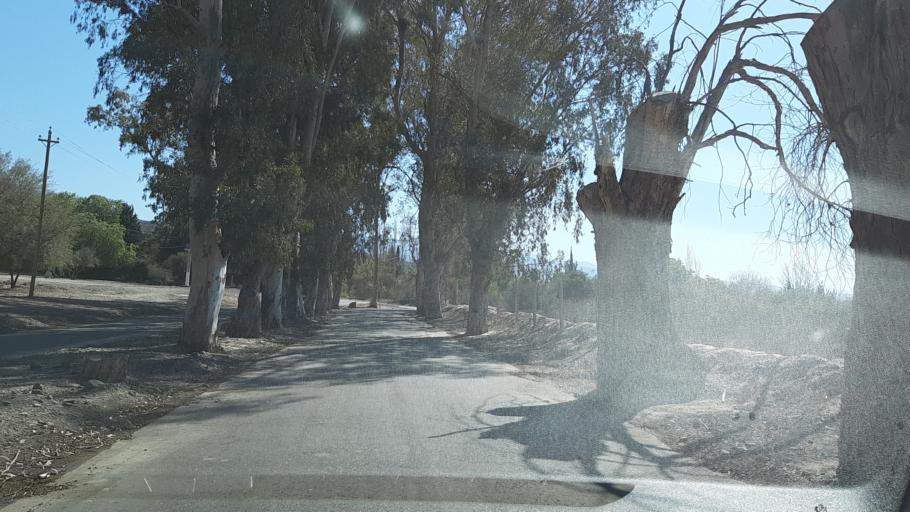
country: AR
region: San Juan
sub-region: Departamento de Zonda
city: Zonda
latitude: -31.5725
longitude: -68.7560
